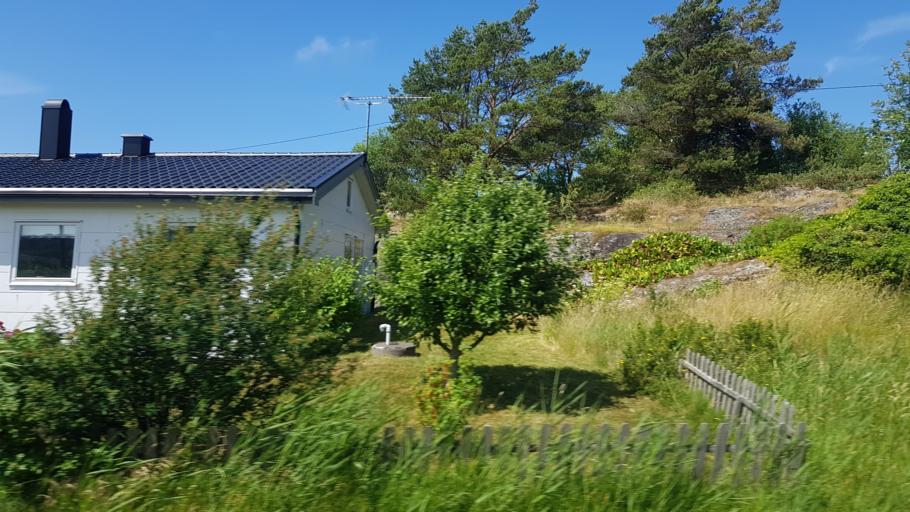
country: SE
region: Vaestra Goetaland
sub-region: Tjorns Kommun
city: Skaerhamn
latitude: 57.9803
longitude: 11.5652
